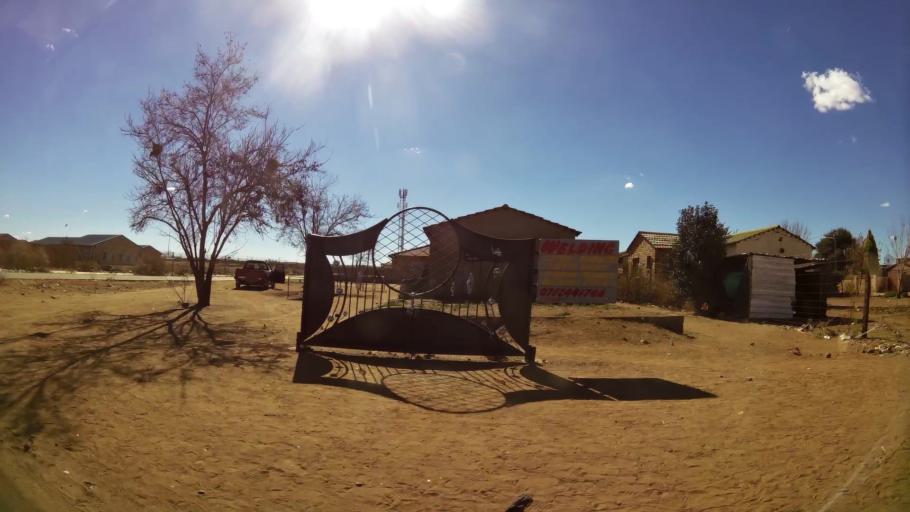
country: ZA
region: North-West
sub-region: Dr Kenneth Kaunda District Municipality
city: Klerksdorp
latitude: -26.8738
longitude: 26.5671
